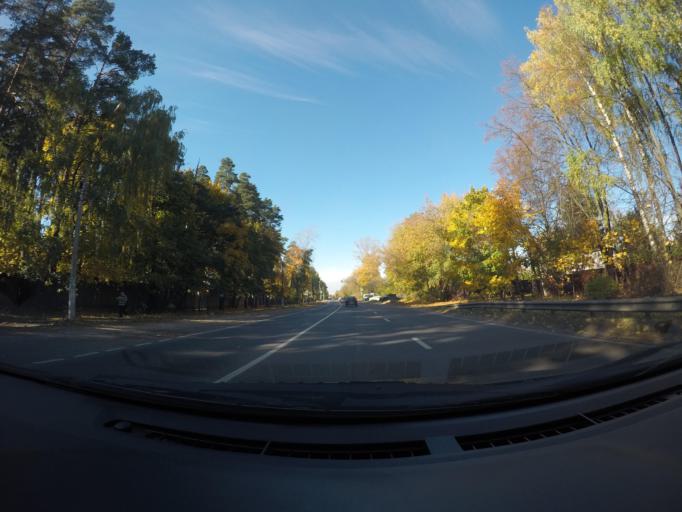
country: RU
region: Moskovskaya
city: Udel'naya
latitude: 55.6278
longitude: 37.9979
